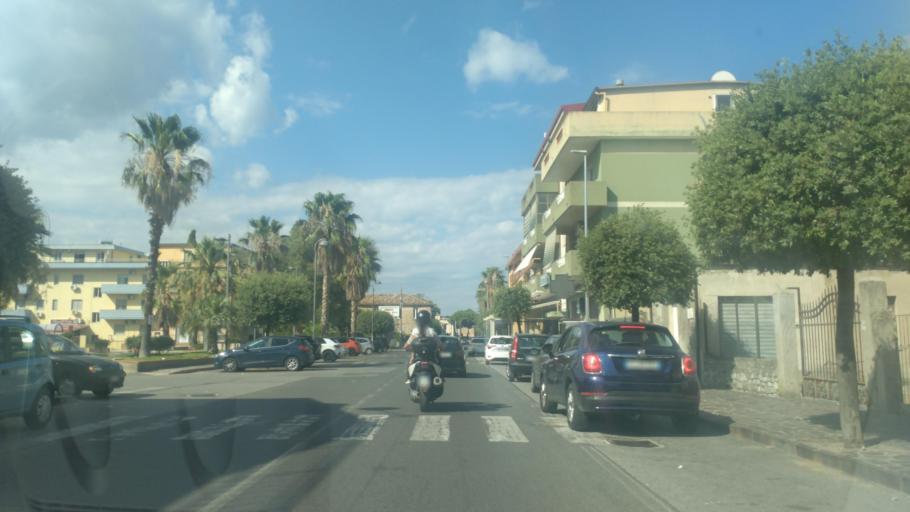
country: IT
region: Calabria
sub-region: Provincia di Catanzaro
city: Montepaone Lido
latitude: 38.7280
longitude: 16.5408
